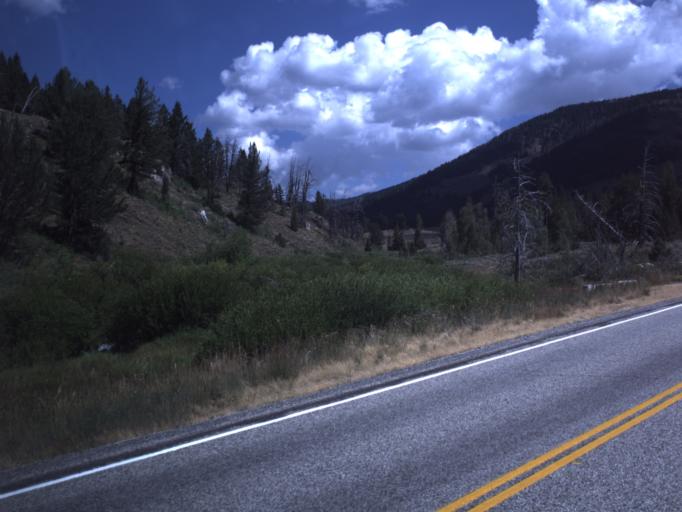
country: US
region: Utah
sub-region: Cache County
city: Richmond
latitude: 41.9615
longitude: -111.5339
